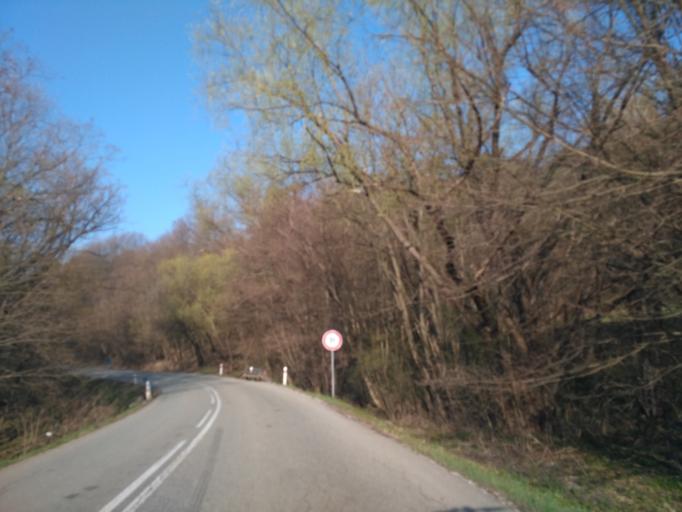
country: SK
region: Kosicky
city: Kosice
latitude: 48.6738
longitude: 21.1256
